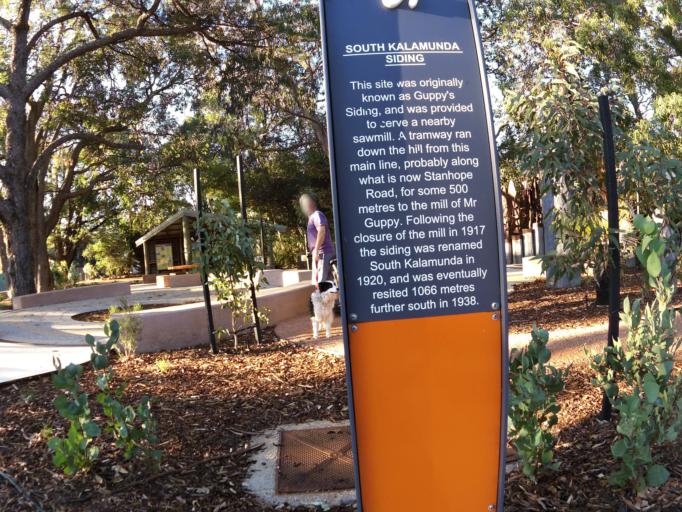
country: AU
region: Western Australia
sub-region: Kalamunda
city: Gooseberry Hill
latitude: -31.9732
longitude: 116.0605
